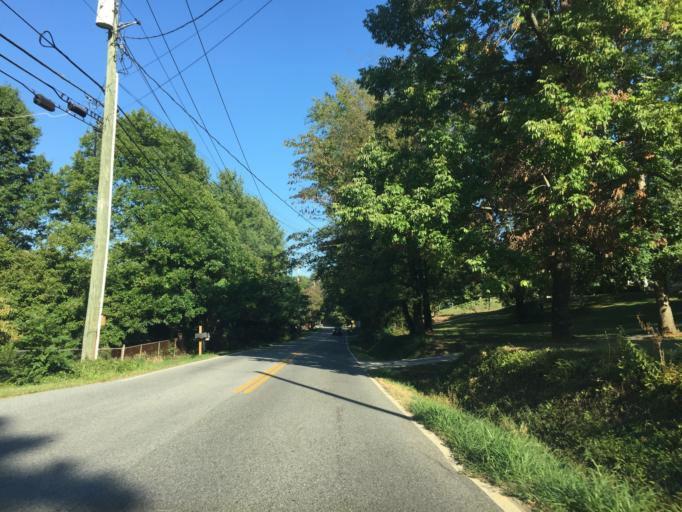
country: US
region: Tennessee
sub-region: Hamilton County
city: Harrison
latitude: 35.1225
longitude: -85.1217
